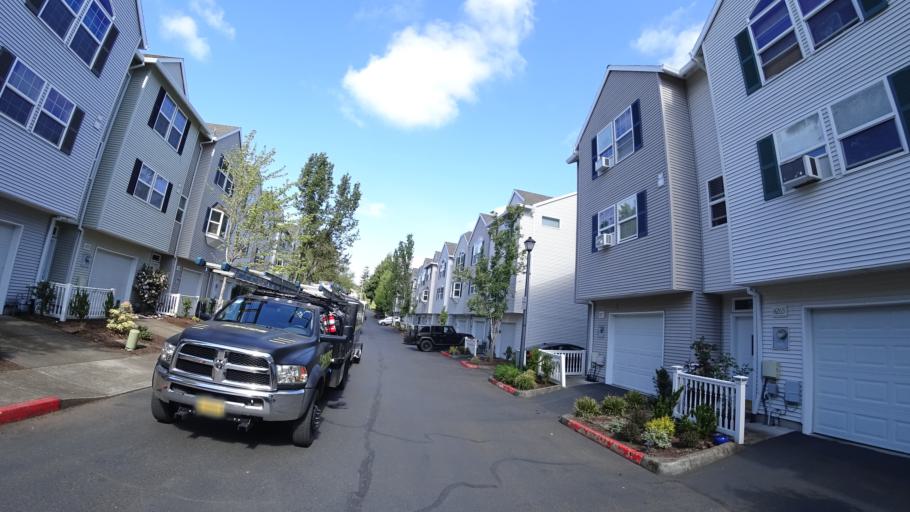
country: US
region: Oregon
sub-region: Washington County
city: King City
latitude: 45.4438
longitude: -122.8245
